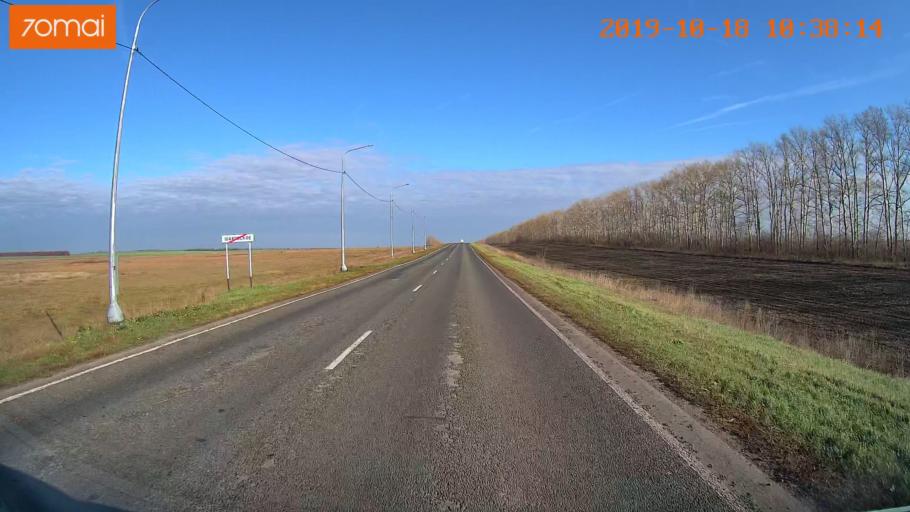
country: RU
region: Tula
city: Kurkino
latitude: 53.5701
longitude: 38.6391
